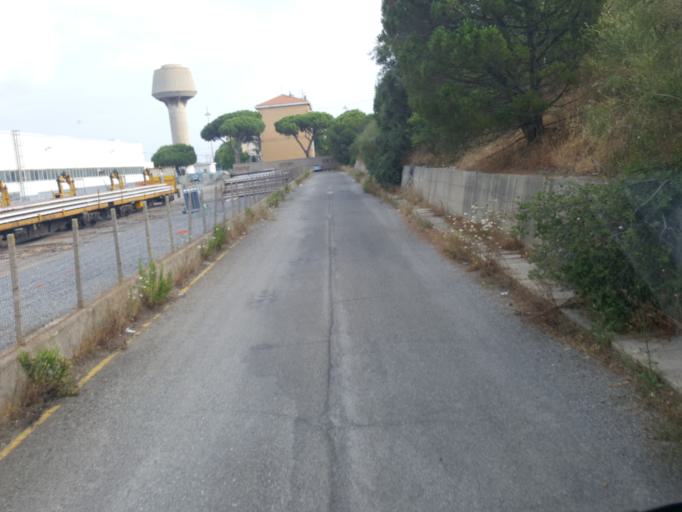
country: IT
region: Latium
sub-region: Citta metropolitana di Roma Capitale
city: Civitavecchia
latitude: 42.1004
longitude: 11.7895
